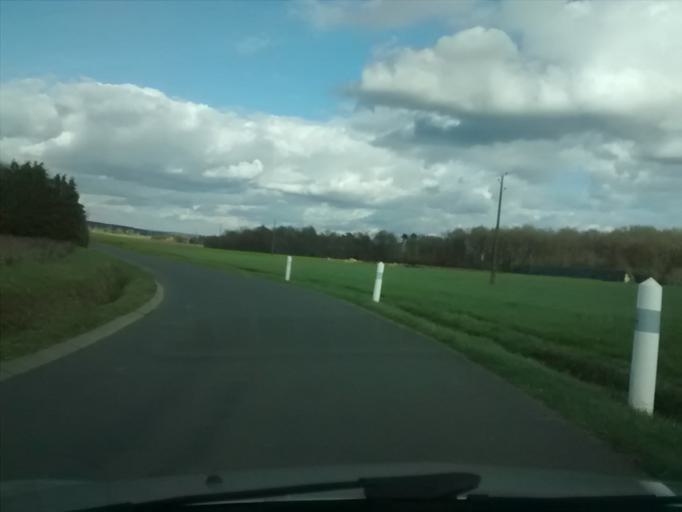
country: FR
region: Pays de la Loire
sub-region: Departement de la Sarthe
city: Bouloire
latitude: 47.9586
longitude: 0.5296
